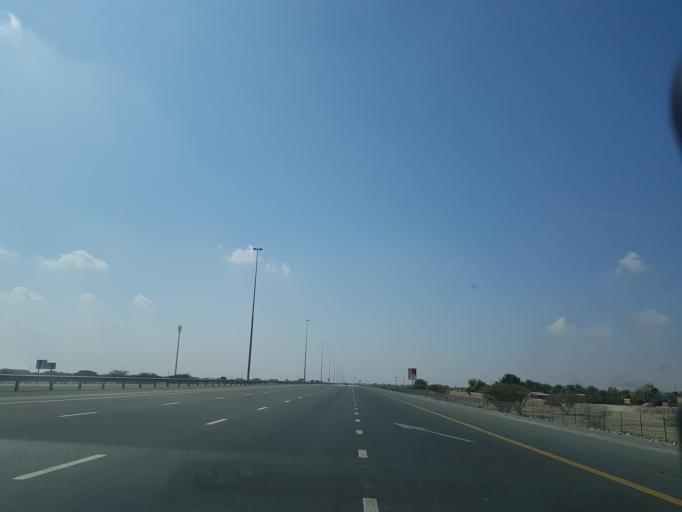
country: AE
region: Ra's al Khaymah
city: Ras al-Khaimah
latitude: 25.7141
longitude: 56.0043
